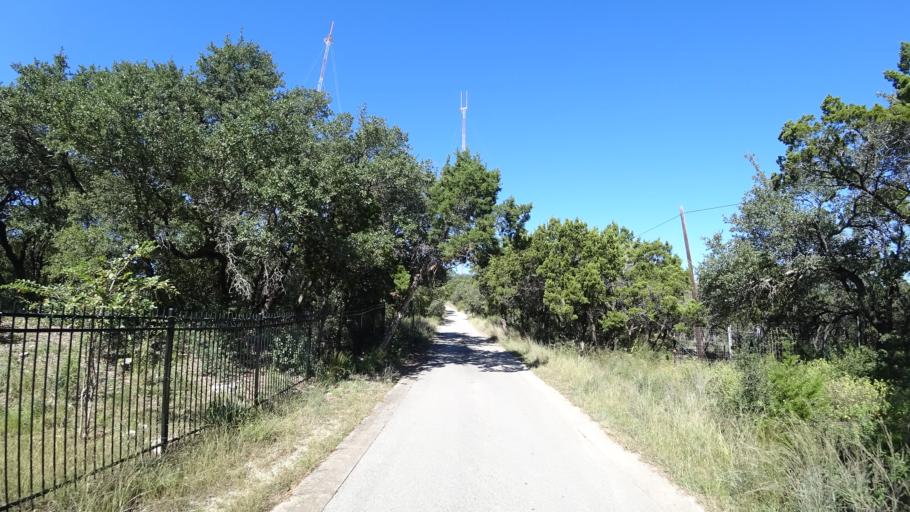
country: US
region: Texas
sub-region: Travis County
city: West Lake Hills
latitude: 30.3229
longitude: -97.7958
